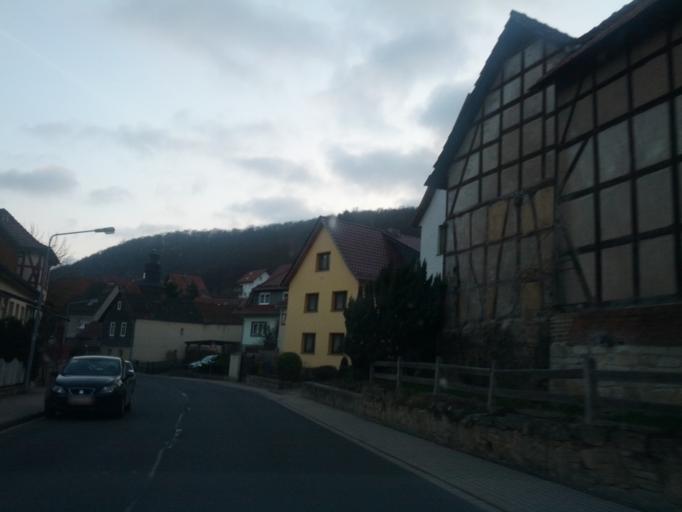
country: DE
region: Thuringia
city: Katharinenberg
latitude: 51.1625
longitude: 10.2497
